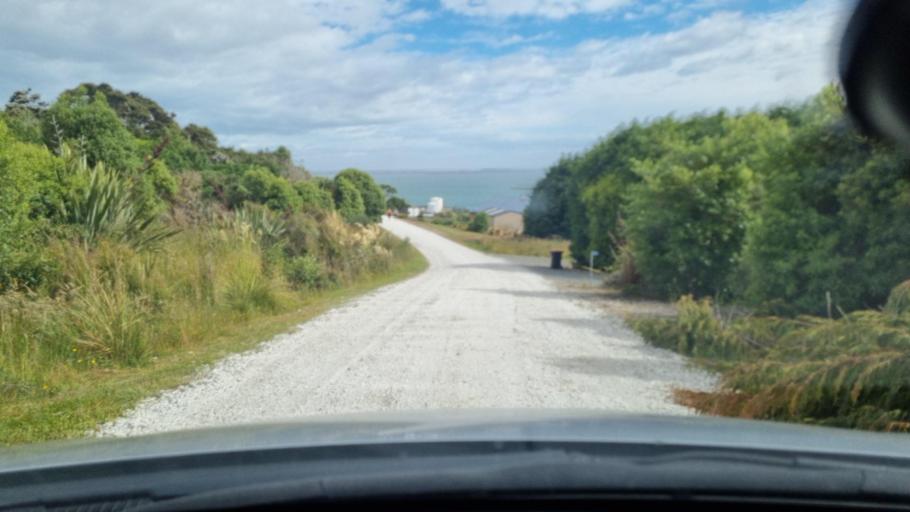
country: NZ
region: Southland
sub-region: Invercargill City
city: Bluff
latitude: -46.6092
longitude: 168.3519
